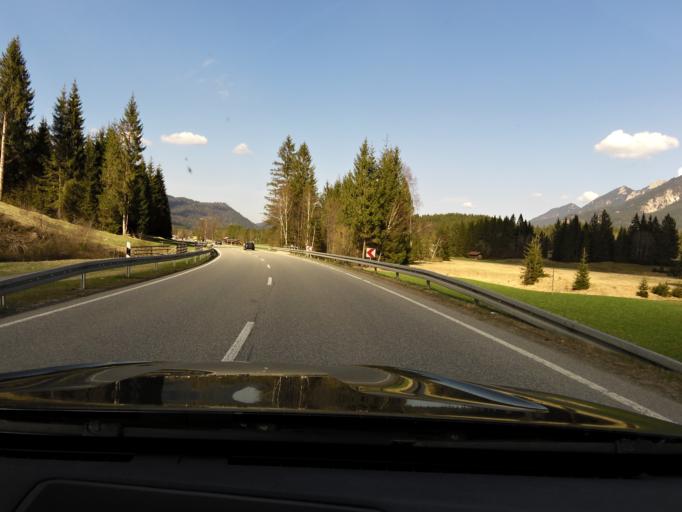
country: DE
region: Bavaria
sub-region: Upper Bavaria
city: Krun
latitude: 47.4866
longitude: 11.2505
